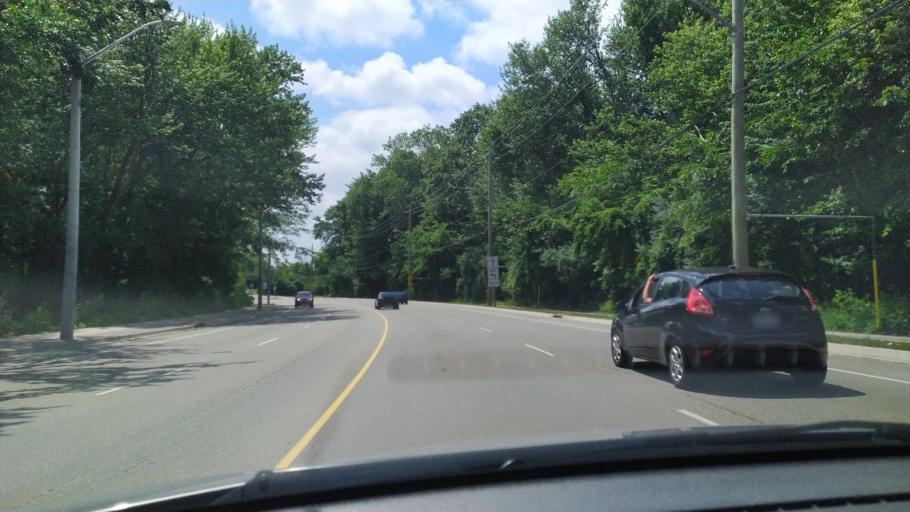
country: CA
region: Ontario
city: Kitchener
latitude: 43.4485
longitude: -80.4562
